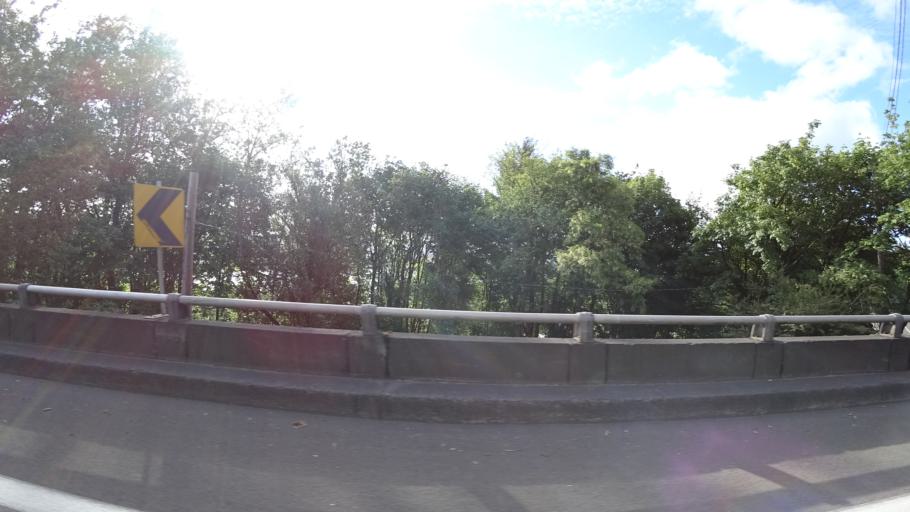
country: US
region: Oregon
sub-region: Multnomah County
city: Portland
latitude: 45.4804
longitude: -122.6801
